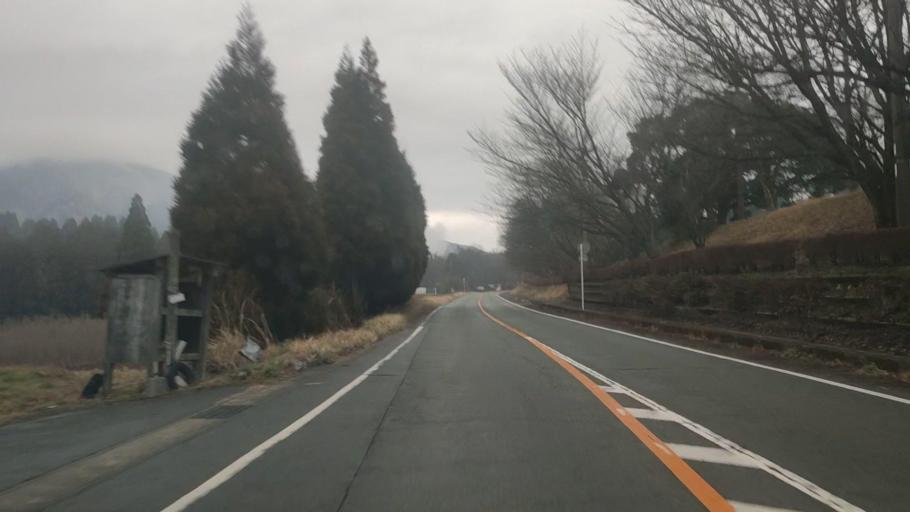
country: JP
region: Kumamoto
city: Aso
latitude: 32.8476
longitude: 131.1487
